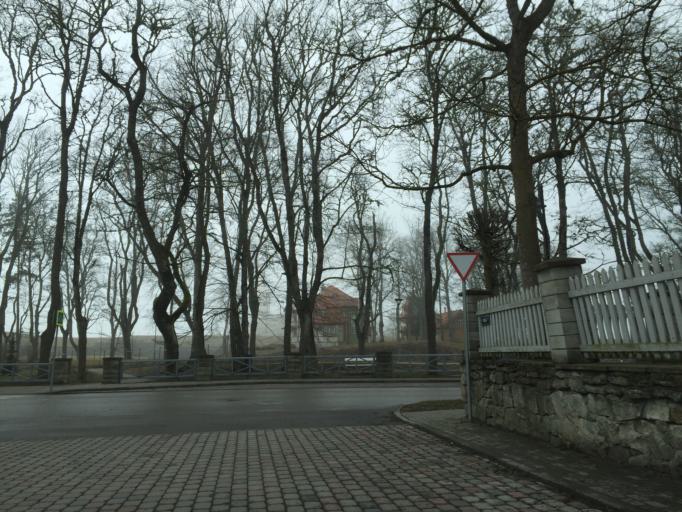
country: EE
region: Saare
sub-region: Kuressaare linn
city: Kuressaare
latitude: 58.2490
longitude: 22.4825
